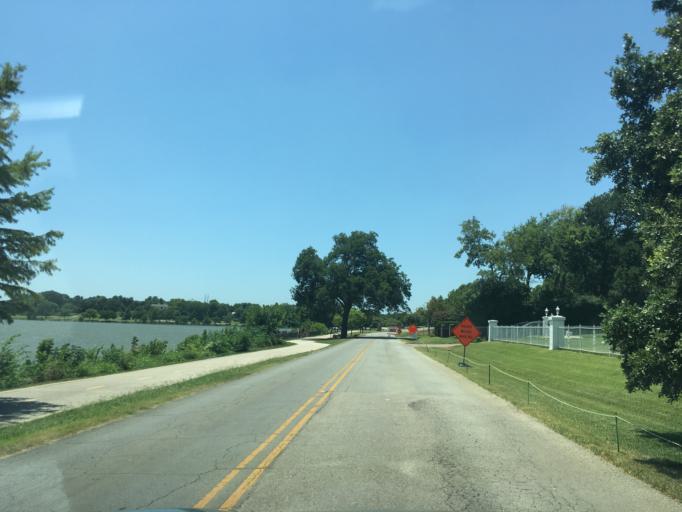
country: US
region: Texas
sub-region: Dallas County
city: Highland Park
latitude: 32.8349
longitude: -96.7263
